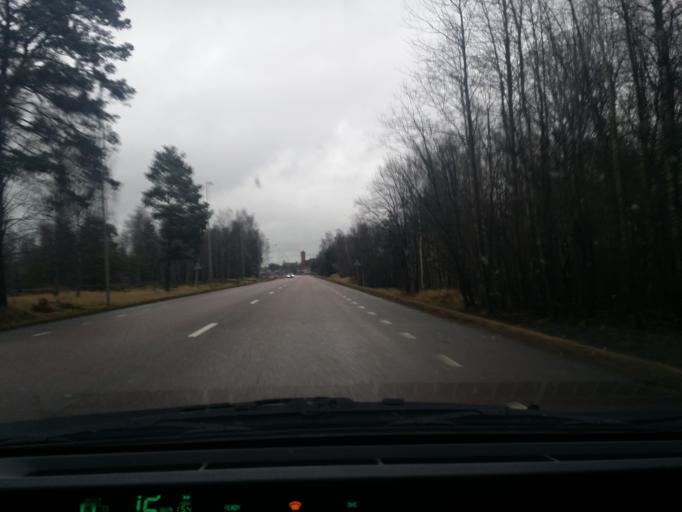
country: SE
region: Vaestmanland
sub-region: Sala Kommun
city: Sala
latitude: 59.9041
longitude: 16.5797
